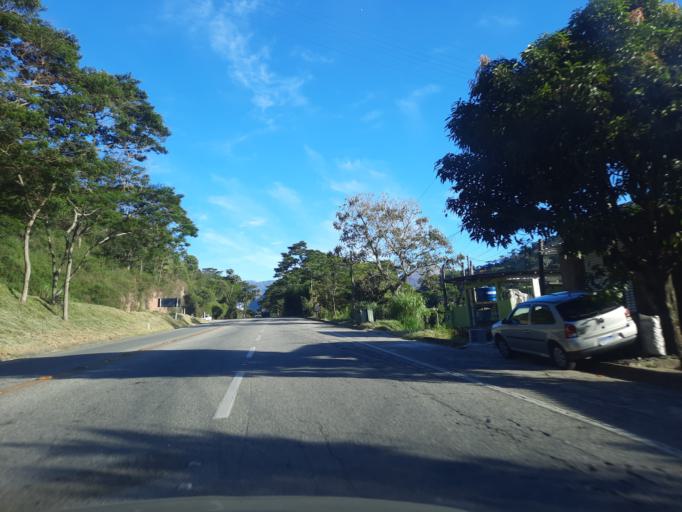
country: BR
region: Rio de Janeiro
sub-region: Petropolis
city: Petropolis
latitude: -22.4090
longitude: -43.1457
